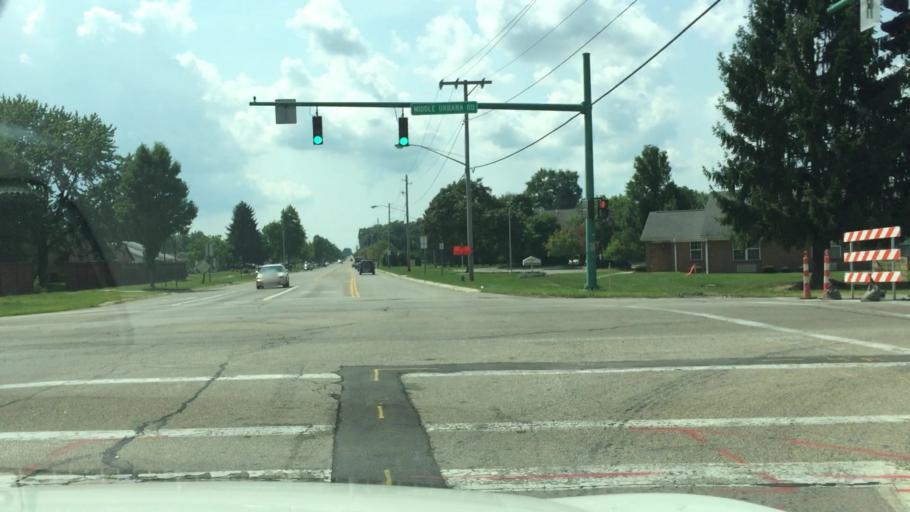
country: US
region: Ohio
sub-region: Clark County
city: Northridge
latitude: 39.9656
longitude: -83.7660
